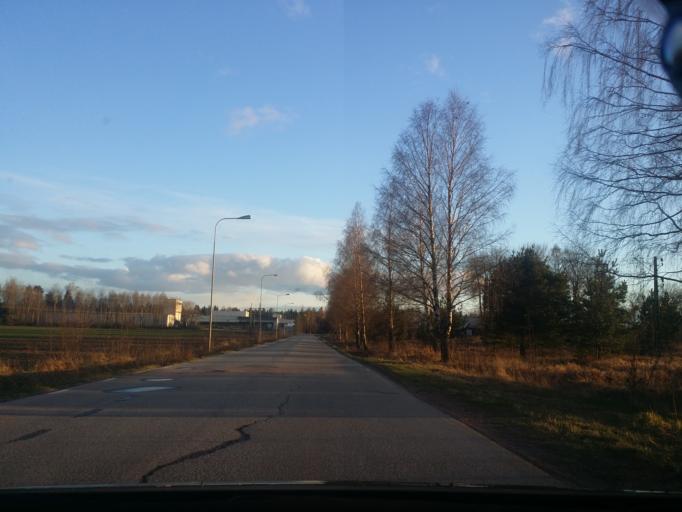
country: SE
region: Vaestmanland
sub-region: Vasteras
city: Hokasen
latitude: 59.6499
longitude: 16.5901
